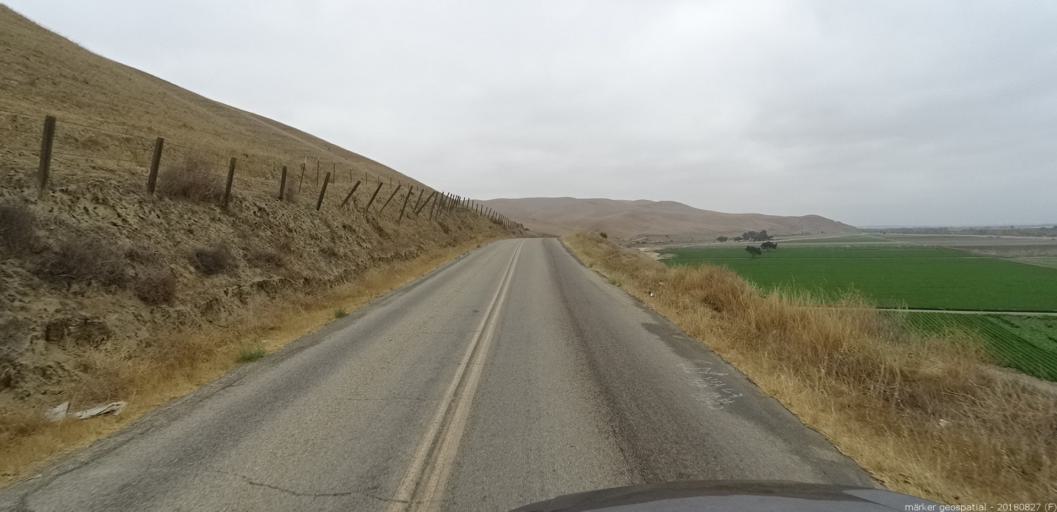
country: US
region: California
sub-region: Monterey County
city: Greenfield
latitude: 36.3371
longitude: -121.1966
